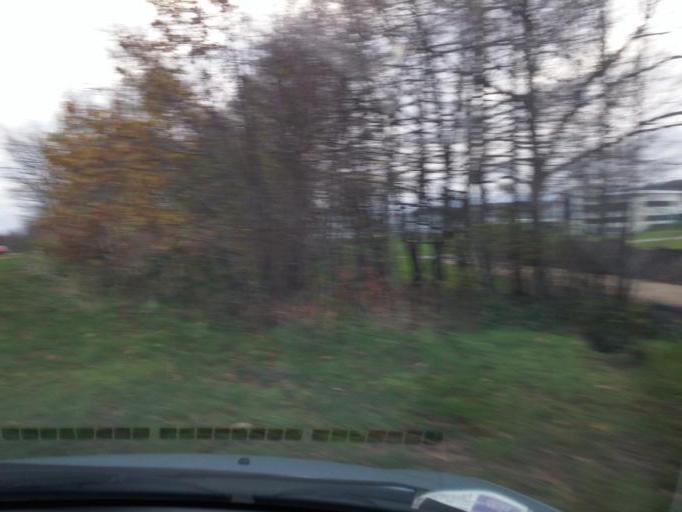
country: DK
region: South Denmark
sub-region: Vejle Kommune
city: Vejle
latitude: 55.7090
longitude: 9.5125
